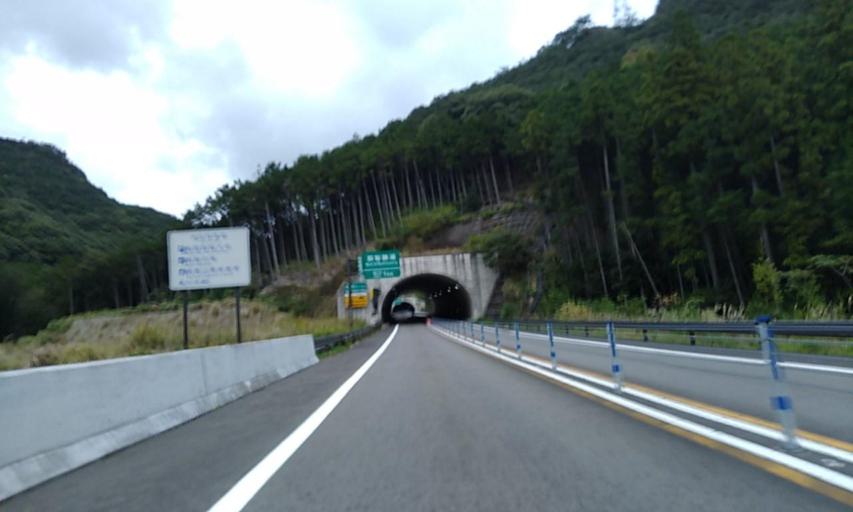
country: JP
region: Wakayama
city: Shingu
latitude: 33.6327
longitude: 135.9240
